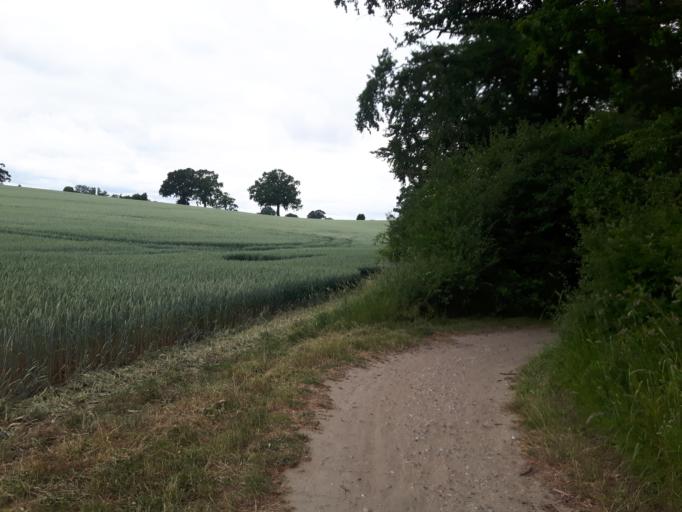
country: DE
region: Schleswig-Holstein
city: Schashagen
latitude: 54.1120
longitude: 10.9143
